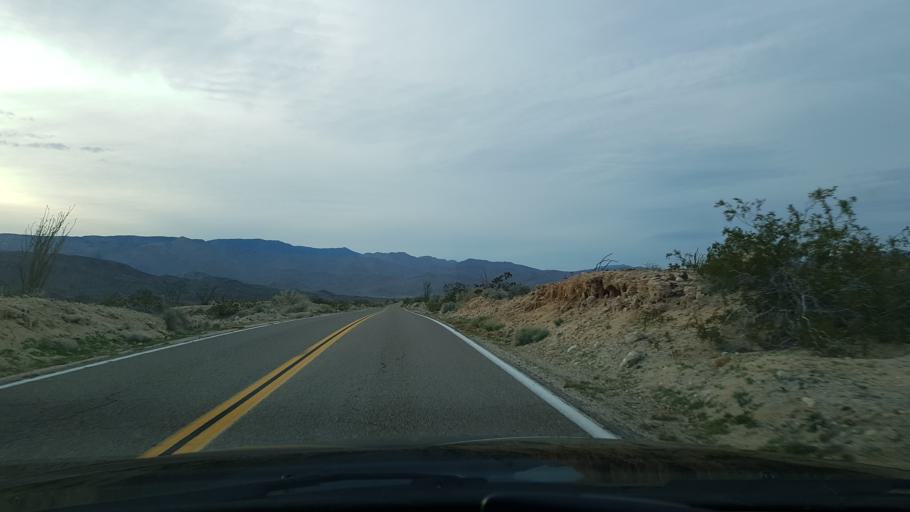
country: MX
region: Baja California
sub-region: Tecate
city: Cereso del Hongo
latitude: 32.8215
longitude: -116.1549
